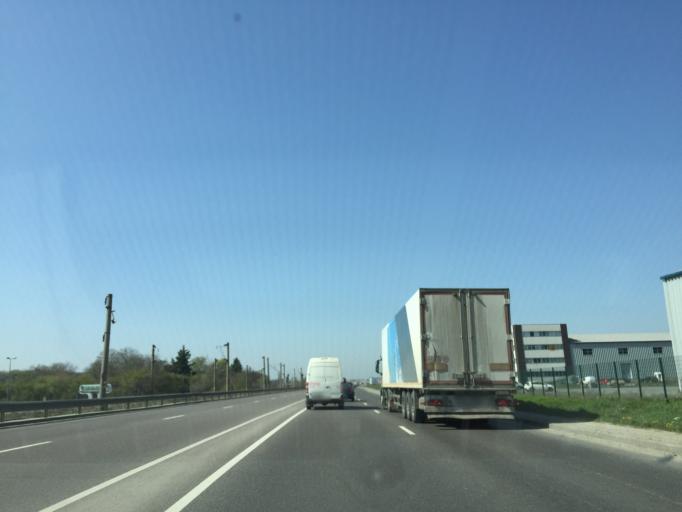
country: RO
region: Ilfov
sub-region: Comuna Otopeni
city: Otopeni
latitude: 44.5389
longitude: 26.0939
